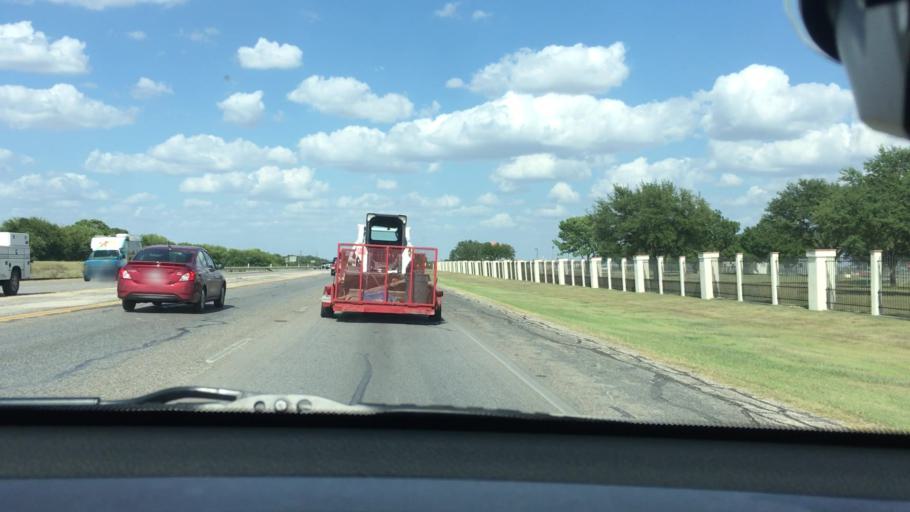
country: US
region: Texas
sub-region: Bexar County
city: Universal City
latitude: 29.5452
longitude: -98.2852
